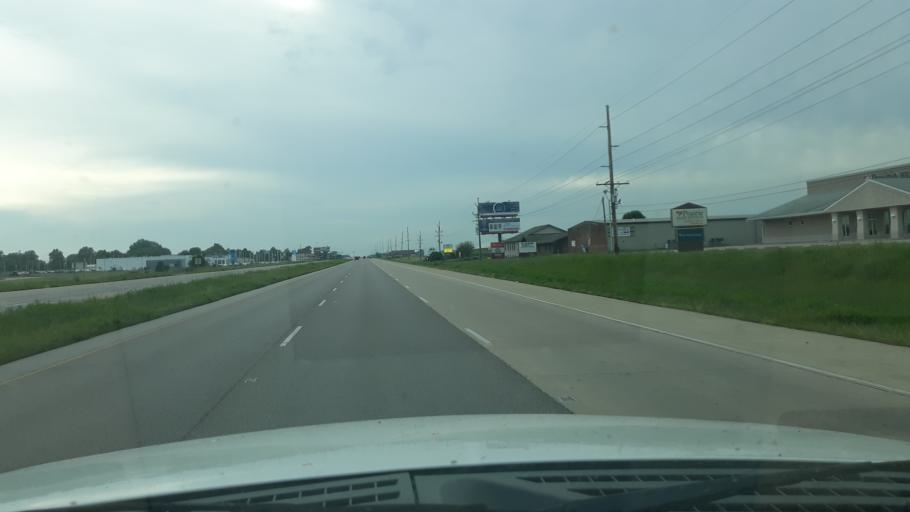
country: US
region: Illinois
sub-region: Williamson County
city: Energy
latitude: 37.7451
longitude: -88.9943
